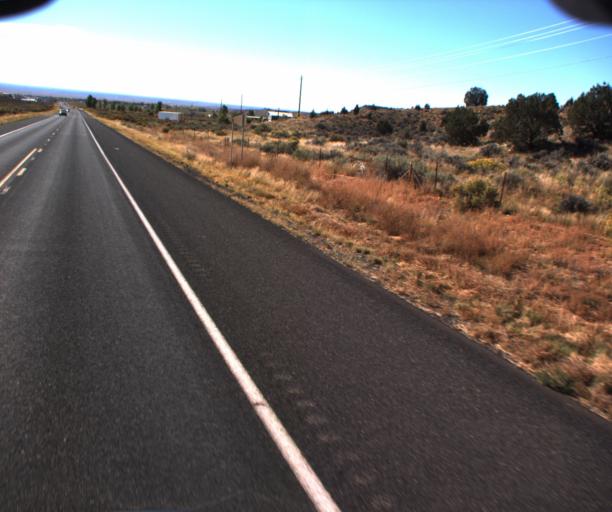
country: US
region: Arizona
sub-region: Coconino County
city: Fredonia
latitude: 36.9851
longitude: -112.5299
